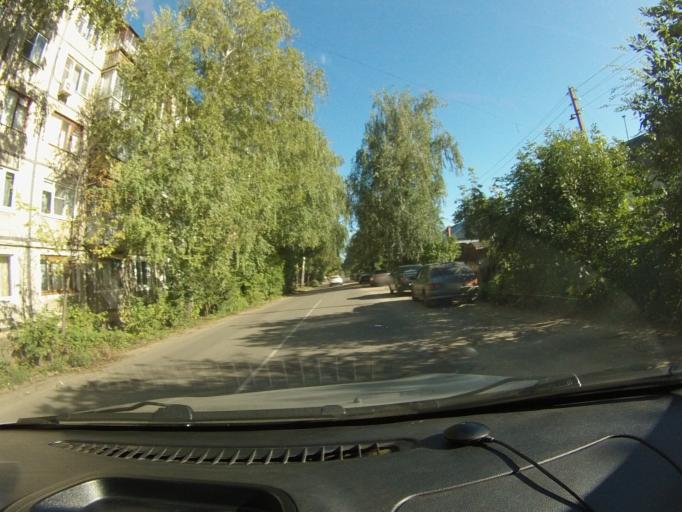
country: RU
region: Tambov
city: Tambov
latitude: 52.7596
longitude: 41.4206
